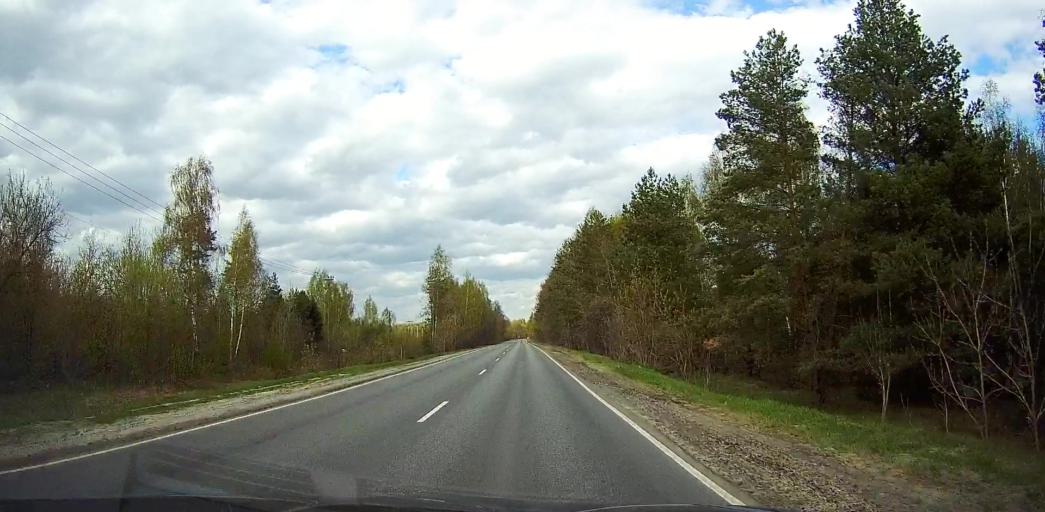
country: RU
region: Moskovskaya
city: Rakhmanovo
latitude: 55.7305
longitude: 38.6314
